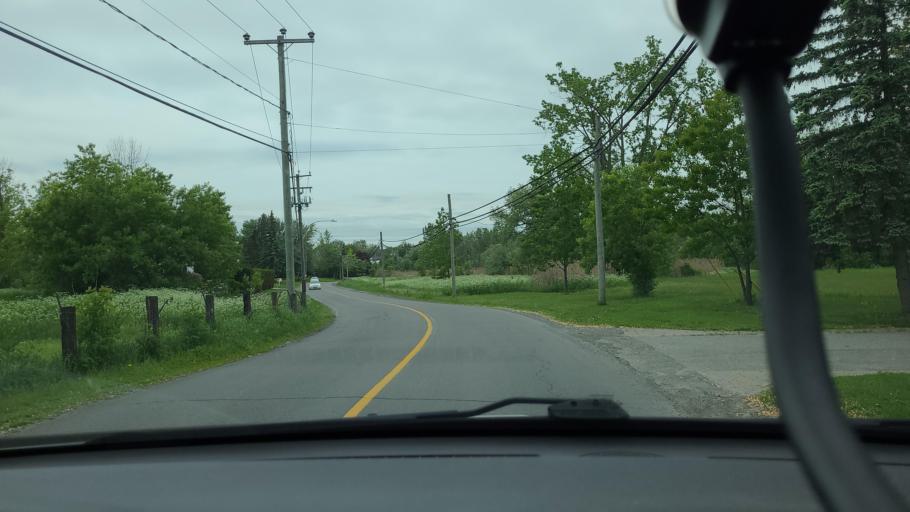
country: CA
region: Quebec
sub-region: Laurentides
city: Rosemere
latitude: 45.6311
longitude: -73.7705
